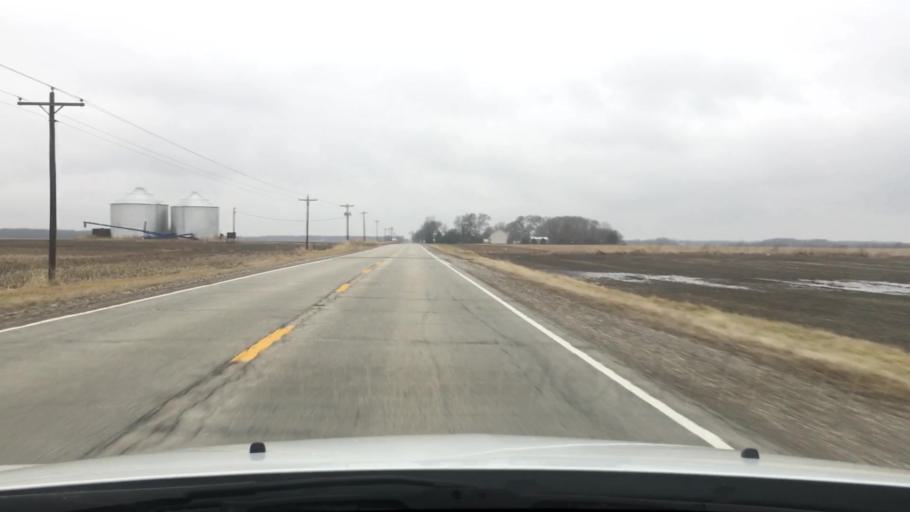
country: US
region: Illinois
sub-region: Iroquois County
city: Watseka
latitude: 40.8888
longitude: -87.7875
